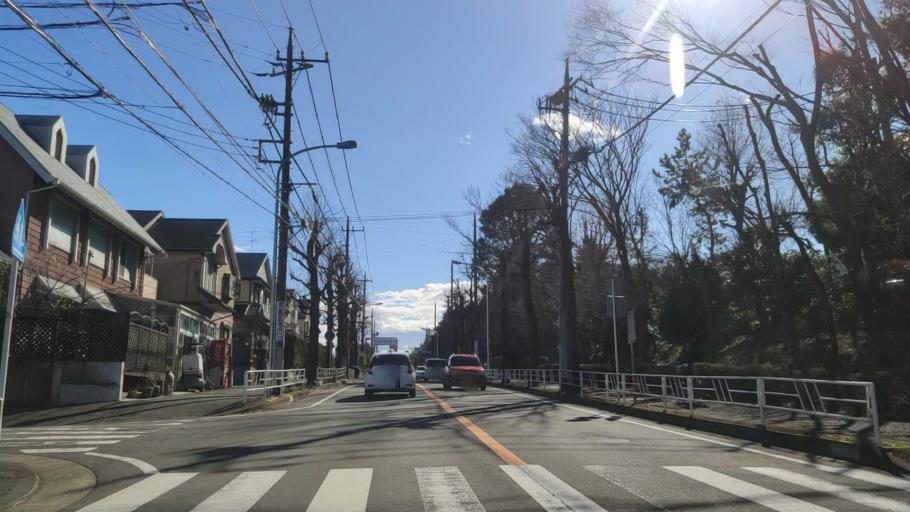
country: JP
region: Kanagawa
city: Minami-rinkan
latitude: 35.5103
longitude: 139.5030
